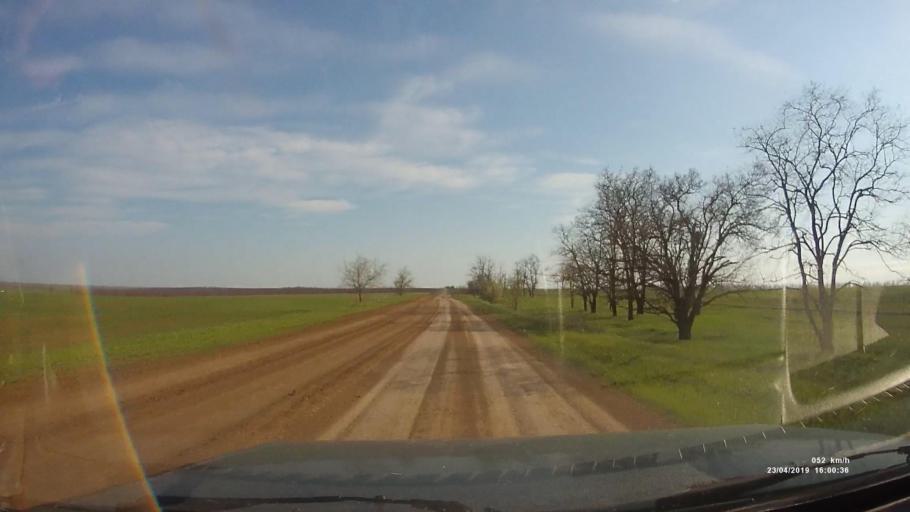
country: RU
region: Rostov
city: Remontnoye
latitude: 46.5080
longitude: 43.1066
